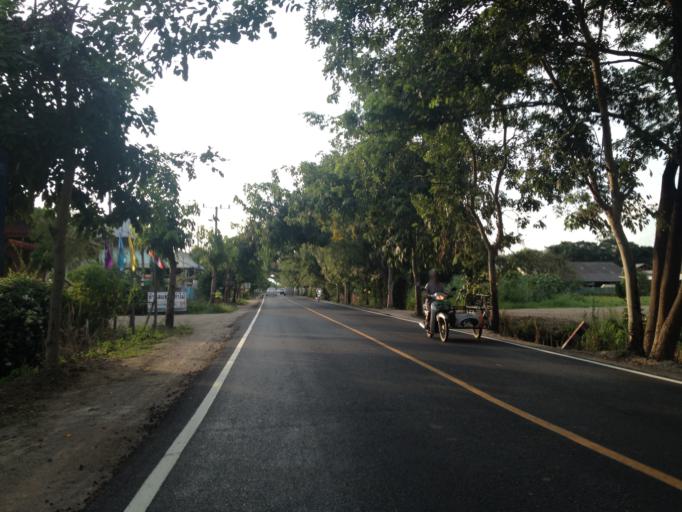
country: TH
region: Chiang Mai
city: Hang Dong
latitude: 18.6830
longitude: 98.9762
